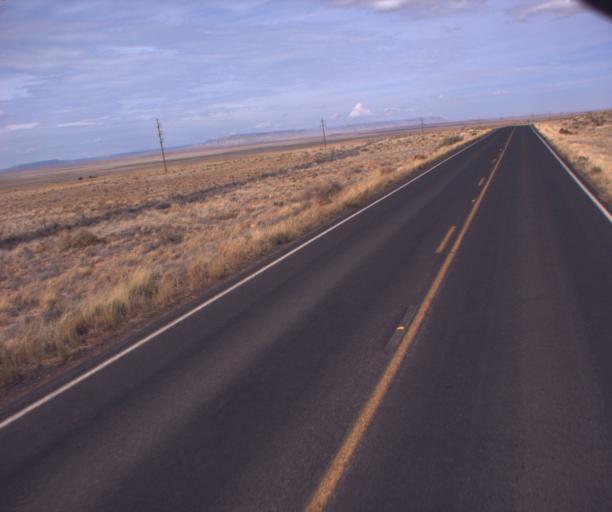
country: US
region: Arizona
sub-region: Apache County
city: Chinle
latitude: 35.9649
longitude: -109.5970
